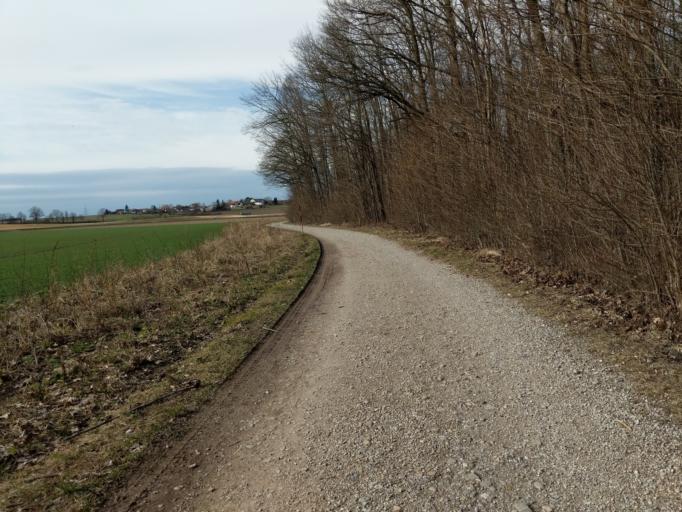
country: DE
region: Bavaria
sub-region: Upper Bavaria
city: Zorneding
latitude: 48.0996
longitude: 11.8386
